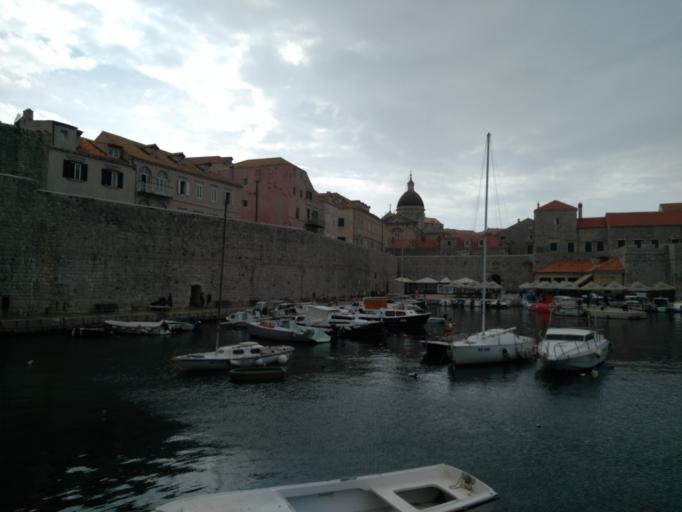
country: HR
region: Dubrovacko-Neretvanska
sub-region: Grad Dubrovnik
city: Dubrovnik
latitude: 42.6403
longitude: 18.1122
